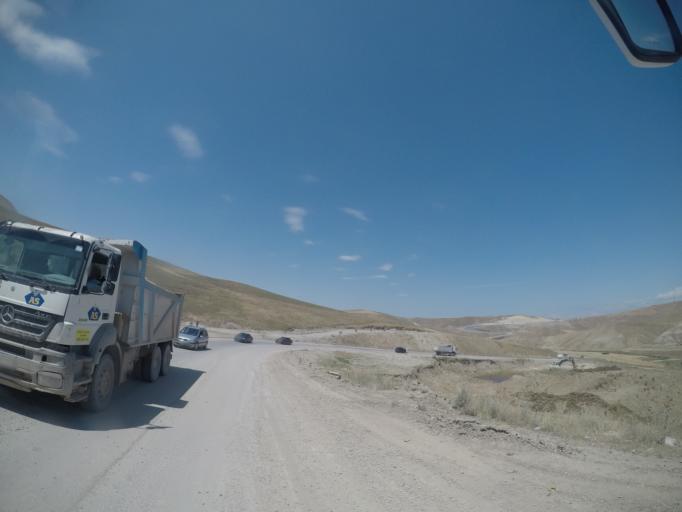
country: AZ
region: Samaxi
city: Shamakhi
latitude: 40.5529
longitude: 48.7659
